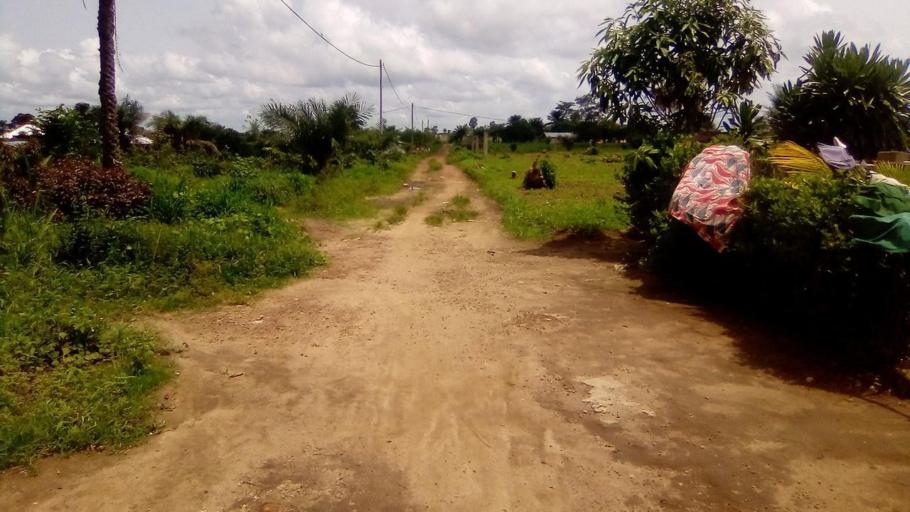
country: SL
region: Southern Province
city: Bo
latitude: 7.9335
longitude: -11.7448
